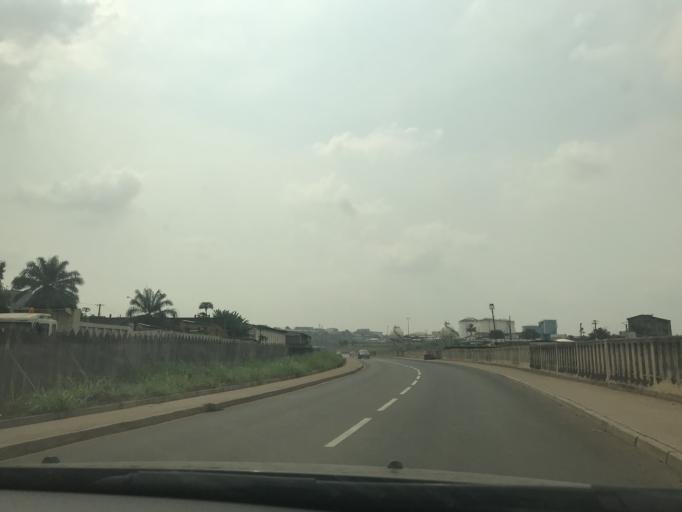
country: CM
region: Centre
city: Yaounde
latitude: 3.8375
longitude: 11.5130
